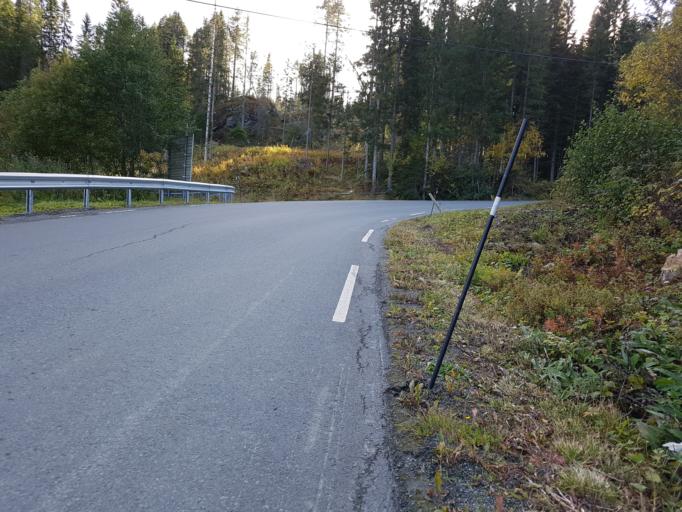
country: NO
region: Sor-Trondelag
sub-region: Klaebu
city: Klaebu
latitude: 63.3462
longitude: 10.5343
